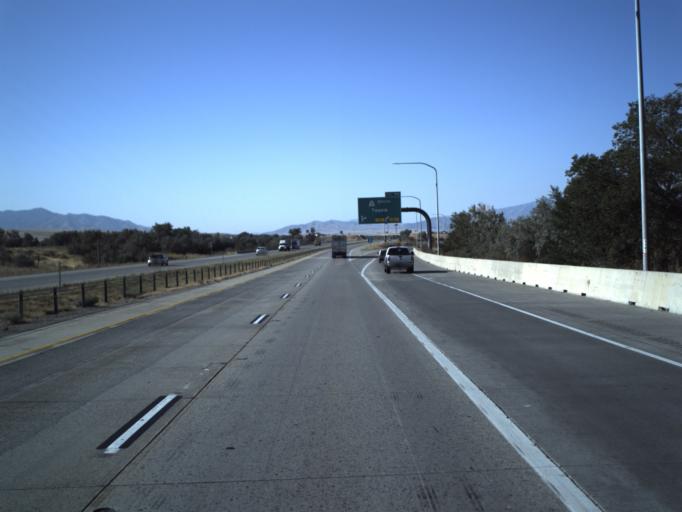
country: US
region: Utah
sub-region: Tooele County
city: Stansbury park
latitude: 40.7018
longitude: -112.2577
